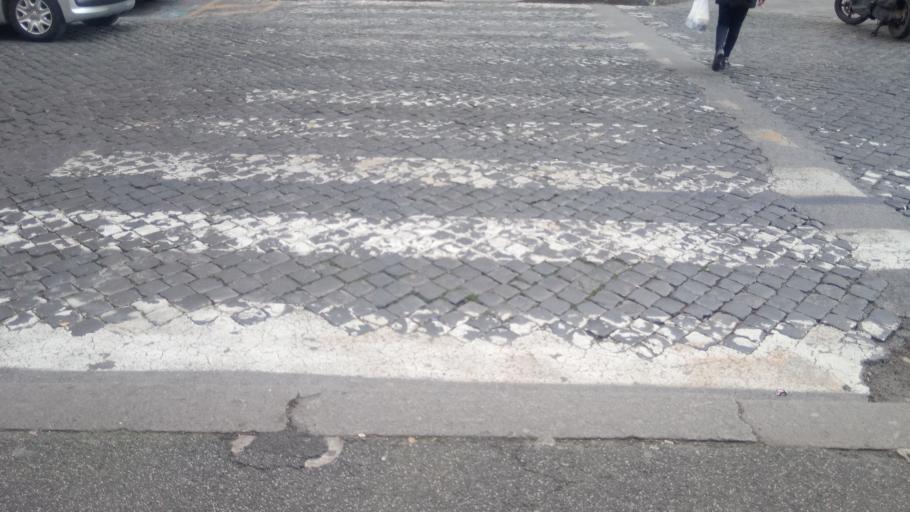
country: IT
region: Latium
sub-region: Citta metropolitana di Roma Capitale
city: Rome
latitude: 41.9010
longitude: 12.5053
